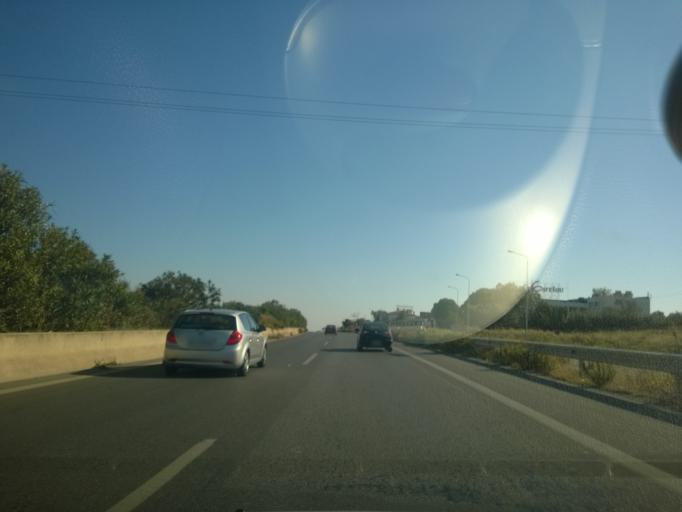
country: GR
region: Central Macedonia
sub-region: Nomos Thessalonikis
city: Kato Scholari
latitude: 40.4410
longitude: 23.0124
